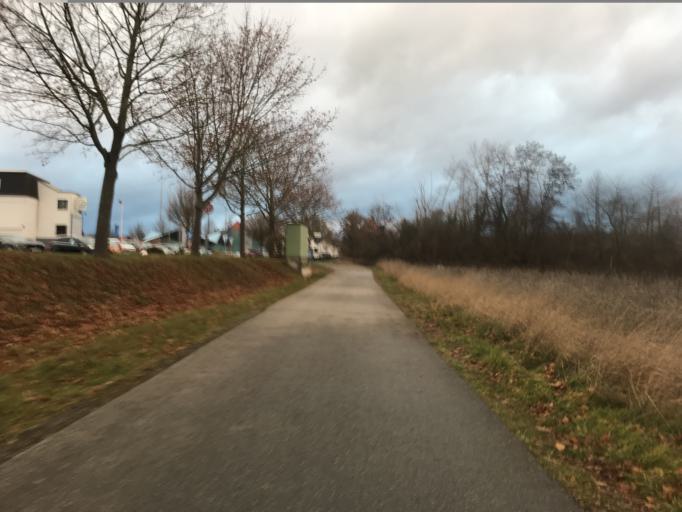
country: DE
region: Hesse
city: Geisenheim
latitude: 49.9658
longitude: 7.9672
